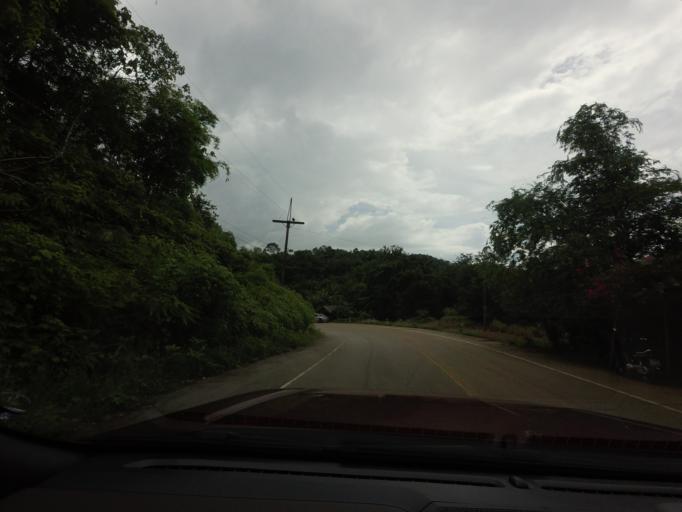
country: TH
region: Narathiwat
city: Sukhirin
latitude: 5.9862
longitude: 101.6854
